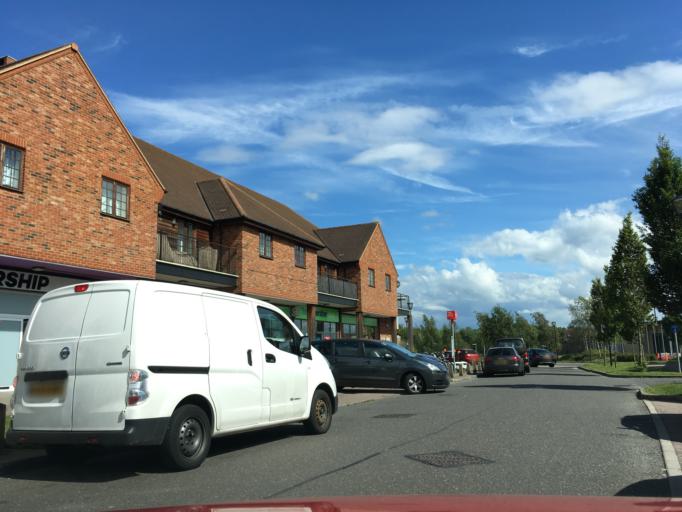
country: GB
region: England
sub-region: Milton Keynes
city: Simpson
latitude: 52.0343
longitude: -0.7108
